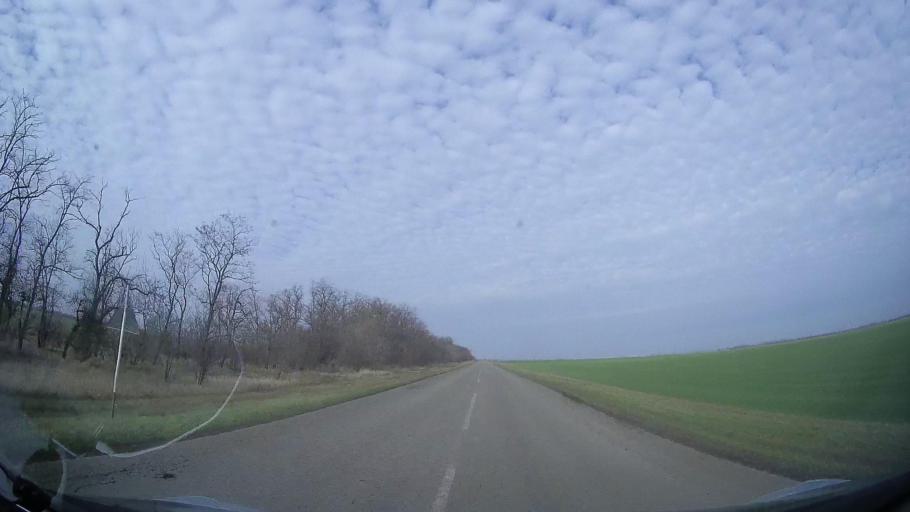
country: RU
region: Rostov
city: Gigant
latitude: 46.9301
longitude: 41.2450
